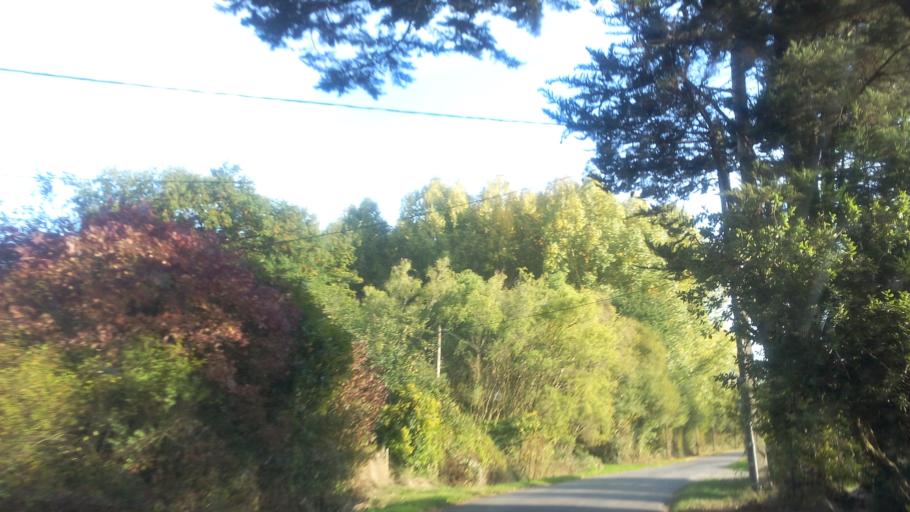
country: FR
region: Brittany
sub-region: Departement du Morbihan
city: Saint-Perreux
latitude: 47.6975
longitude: -2.1101
